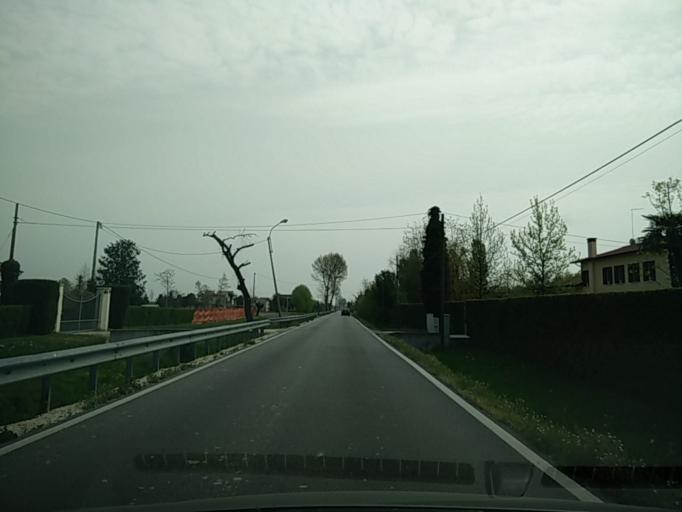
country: IT
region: Veneto
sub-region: Provincia di Venezia
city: Caltana
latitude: 45.4766
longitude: 12.0436
